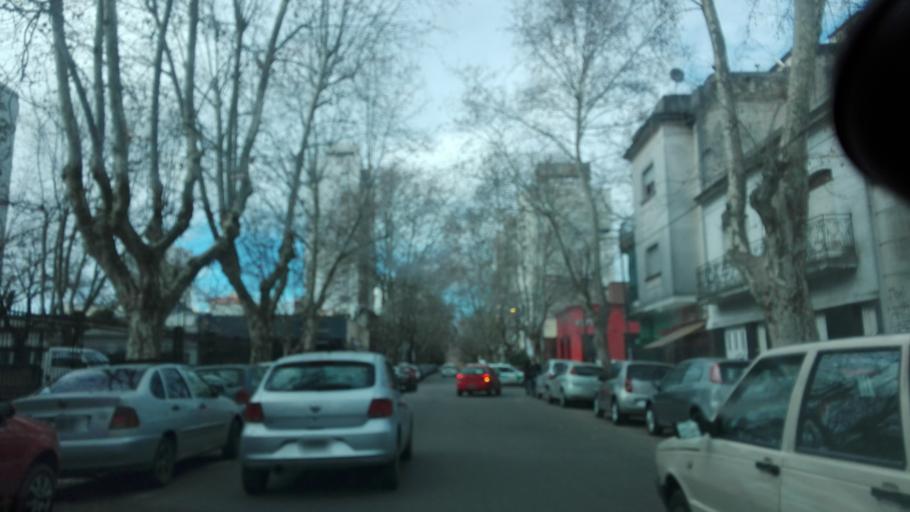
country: AR
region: Buenos Aires
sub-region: Partido de La Plata
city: La Plata
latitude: -34.9248
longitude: -57.9525
